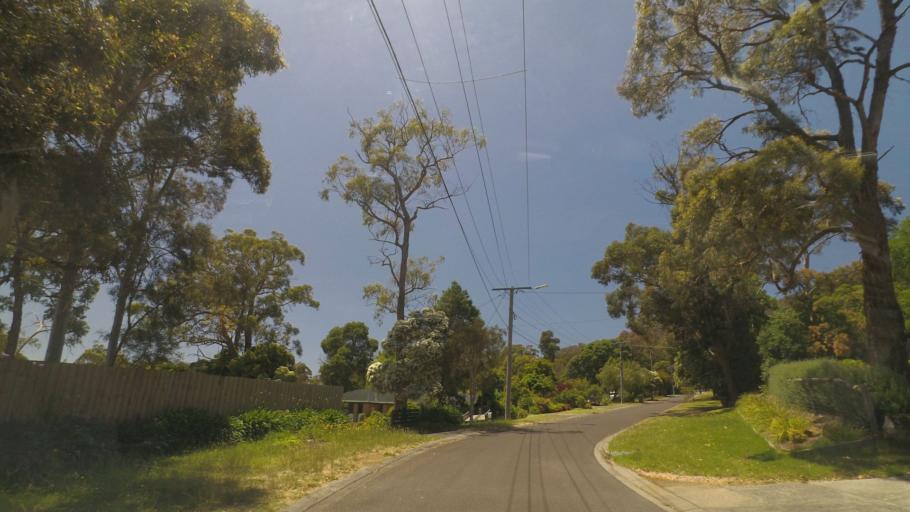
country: AU
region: Victoria
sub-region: Yarra Ranges
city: Montrose
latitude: -37.8171
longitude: 145.3455
